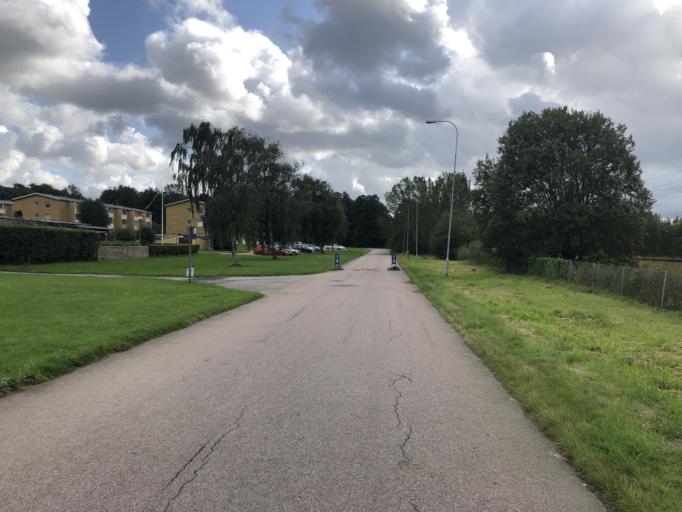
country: SE
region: Vaestra Goetaland
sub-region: Goteborg
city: Goeteborg
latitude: 57.7631
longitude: 11.9445
